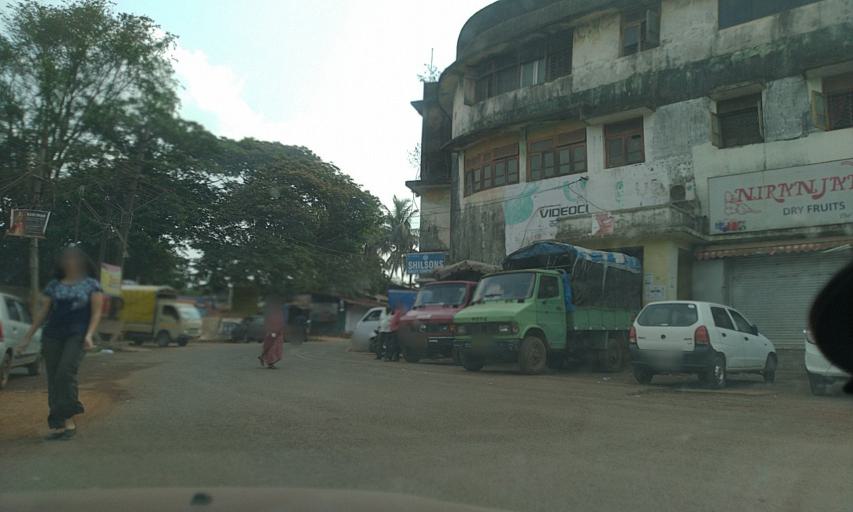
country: IN
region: Goa
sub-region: North Goa
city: Ponda
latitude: 15.4028
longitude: 74.0077
